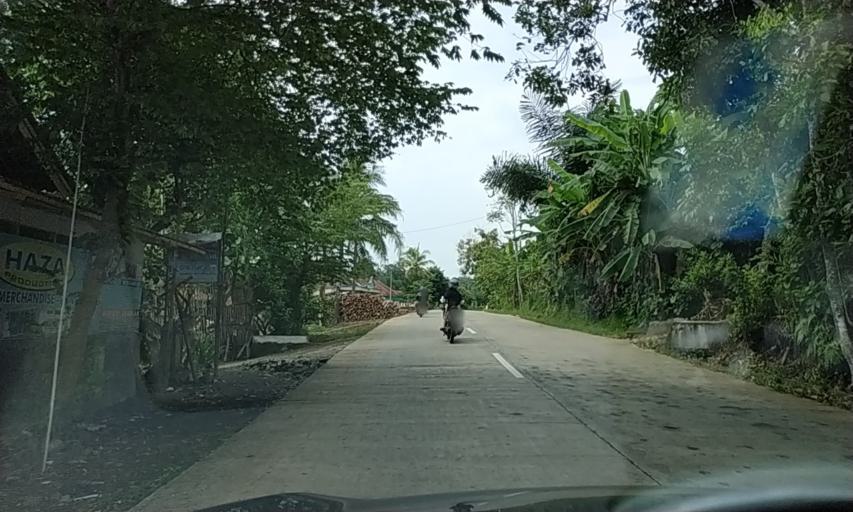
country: ID
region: Central Java
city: Winangun
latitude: -7.3659
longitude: 108.6999
